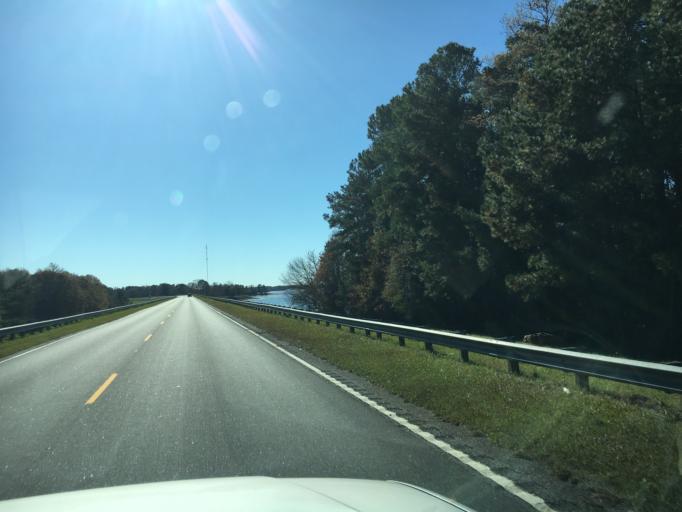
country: US
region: Georgia
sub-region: Hart County
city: Hartwell
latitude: 34.3735
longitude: -82.8134
